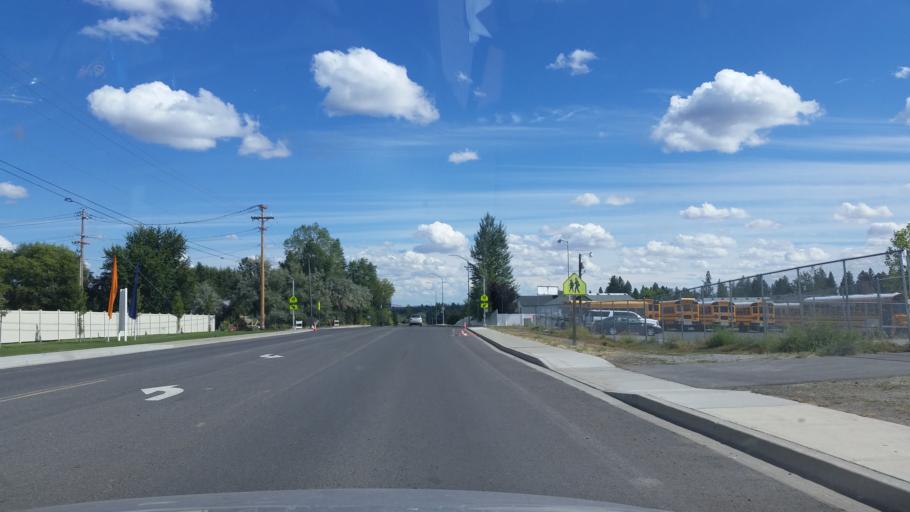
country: US
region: Washington
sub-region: Spokane County
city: Cheney
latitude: 47.5073
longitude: -117.5769
